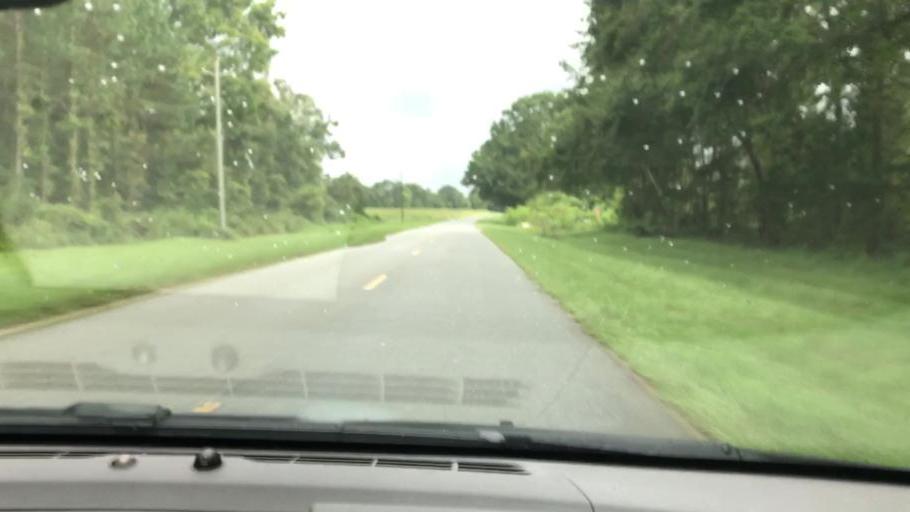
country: US
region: Georgia
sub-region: Clay County
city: Fort Gaines
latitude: 31.7160
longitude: -85.0660
